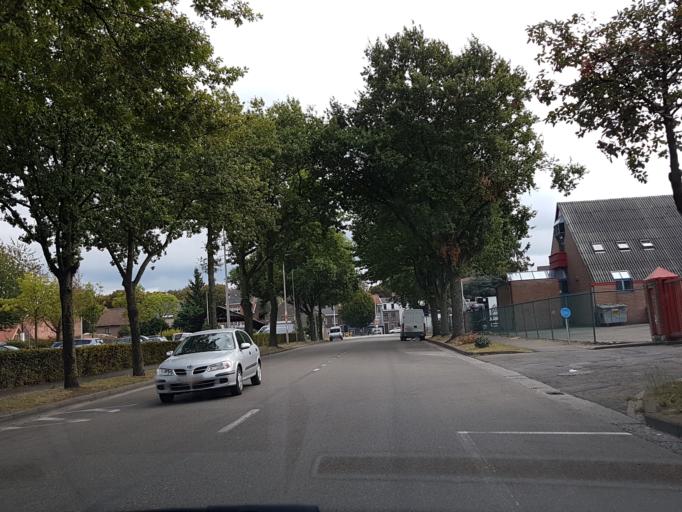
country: BE
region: Flanders
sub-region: Provincie Limburg
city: Sint-Truiden
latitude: 50.8212
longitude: 5.1917
